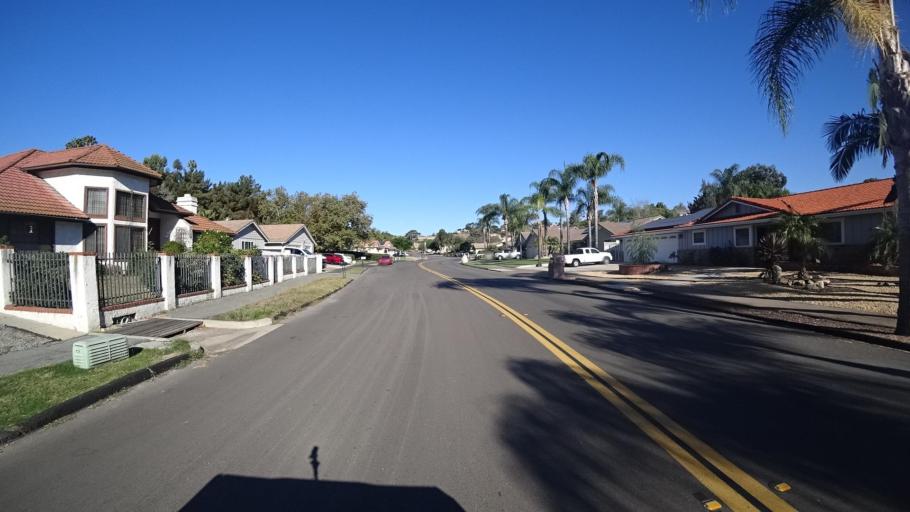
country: US
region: California
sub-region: San Diego County
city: Bonita
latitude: 32.6821
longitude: -117.0176
